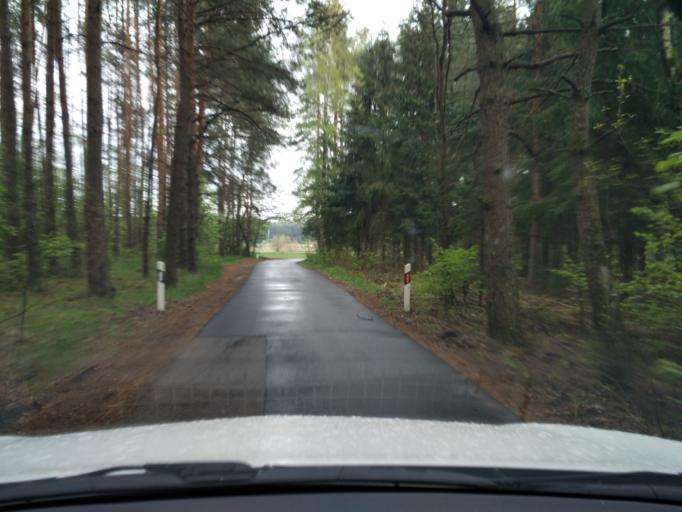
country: LT
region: Vilnius County
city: Rasos
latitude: 54.7399
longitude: 25.3988
